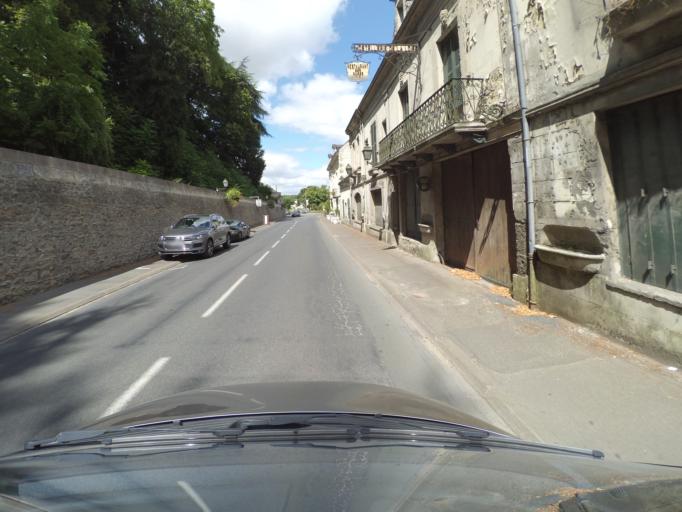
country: FR
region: Pays de la Loire
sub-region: Departement de Maine-et-Loire
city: Gennes
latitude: 47.3427
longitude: -0.2320
